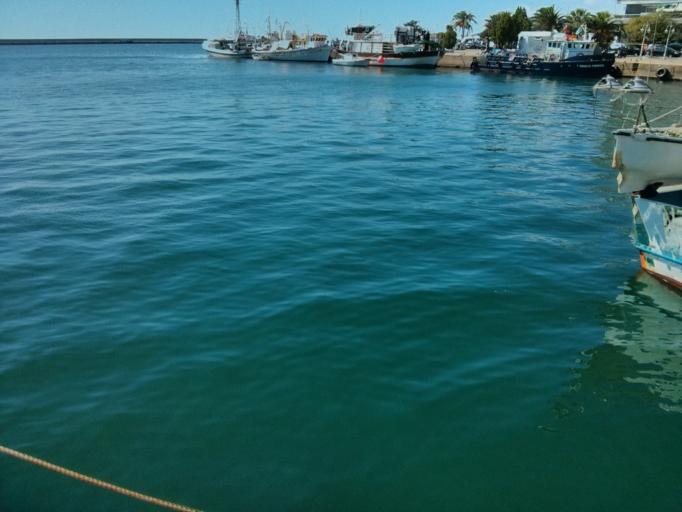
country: GR
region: East Macedonia and Thrace
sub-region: Nomos Kavalas
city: Kavala
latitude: 40.9361
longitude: 24.4103
